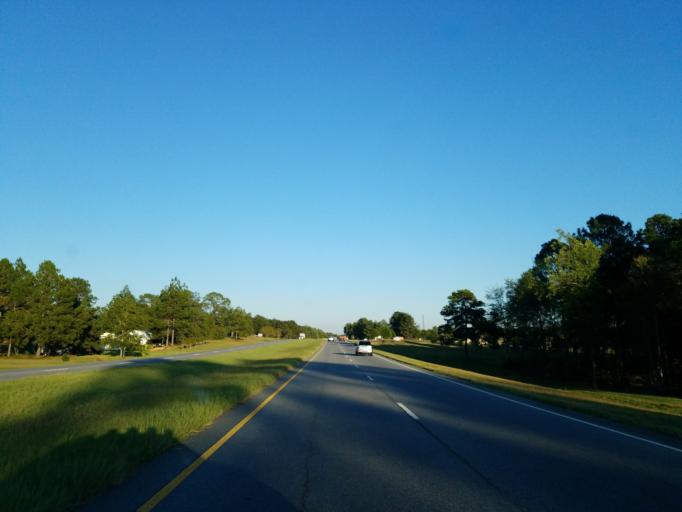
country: US
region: Georgia
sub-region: Worth County
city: Sylvester
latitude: 31.5094
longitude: -83.7456
